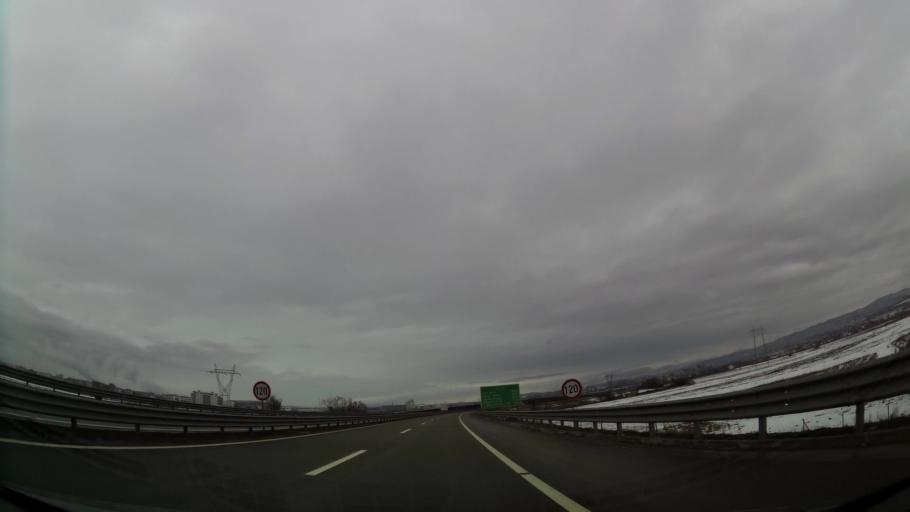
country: XK
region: Pristina
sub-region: Kosovo Polje
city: Kosovo Polje
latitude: 42.6281
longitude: 21.1175
